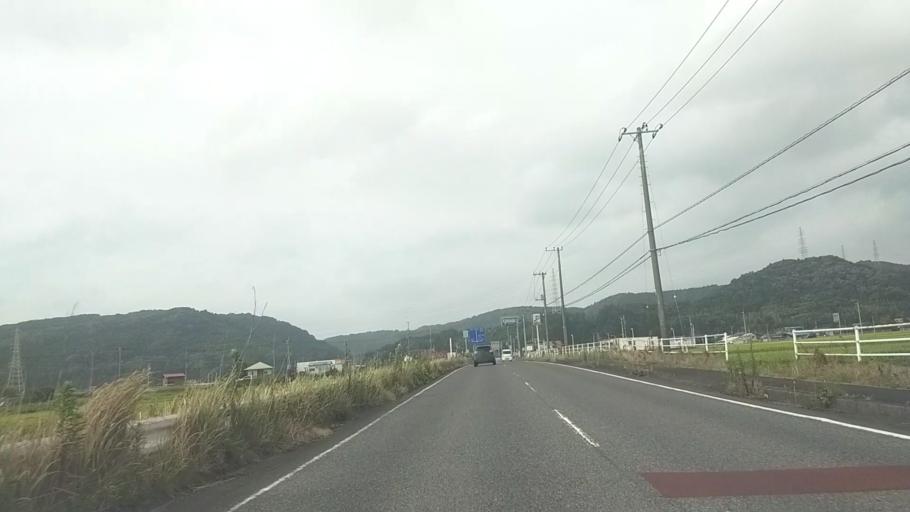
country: JP
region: Chiba
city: Kisarazu
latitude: 35.3003
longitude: 139.9869
